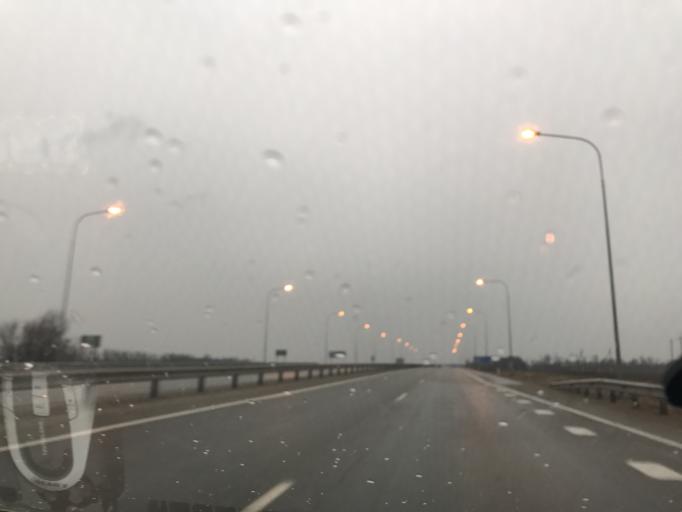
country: RU
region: Krasnodarskiy
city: Pavlovskaya
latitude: 46.2538
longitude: 39.8317
